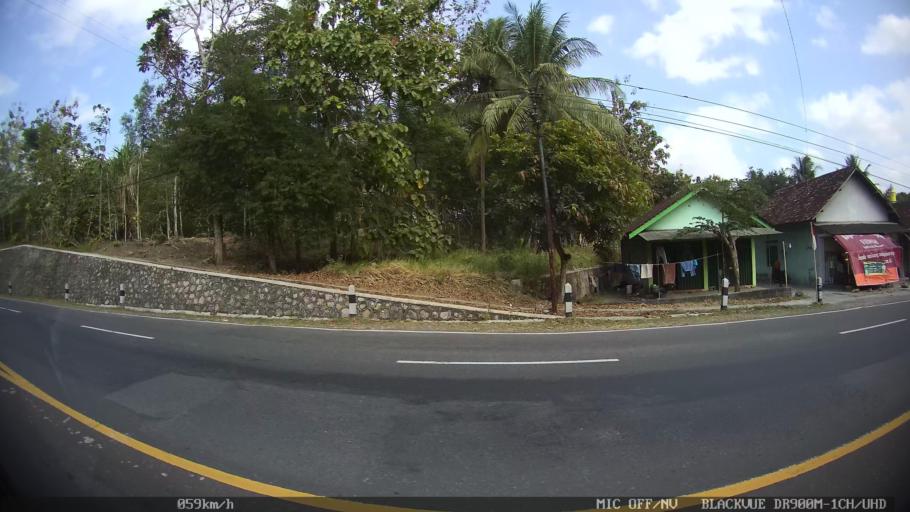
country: ID
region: Daerah Istimewa Yogyakarta
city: Srandakan
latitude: -7.8489
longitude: 110.2176
